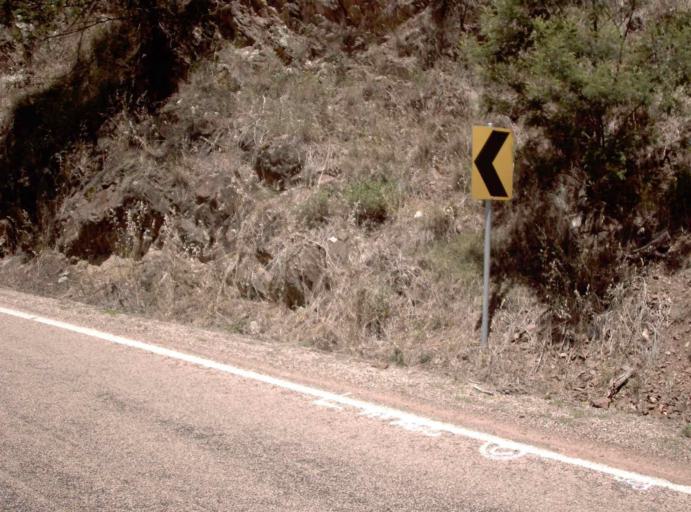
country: AU
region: Victoria
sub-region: East Gippsland
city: Bairnsdale
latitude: -37.4193
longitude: 147.8324
